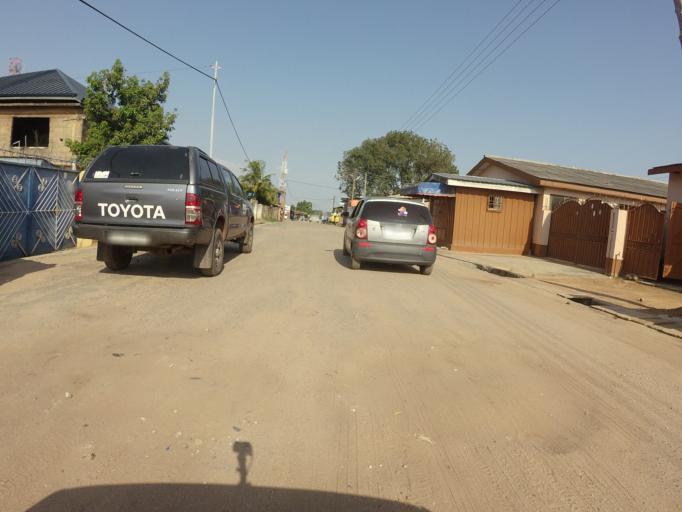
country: GH
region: Greater Accra
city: Dome
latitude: 5.6127
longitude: -0.2415
